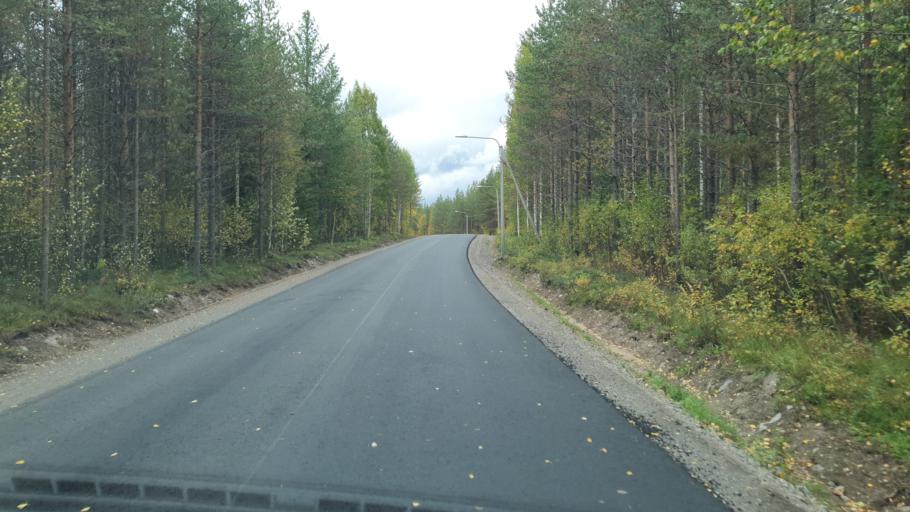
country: FI
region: Lapland
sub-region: Rovaniemi
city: Rovaniemi
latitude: 66.4230
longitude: 25.4033
